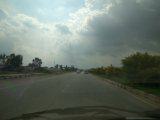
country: IN
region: Karnataka
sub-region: Kolar
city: Kolar
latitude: 13.1280
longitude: 77.9962
